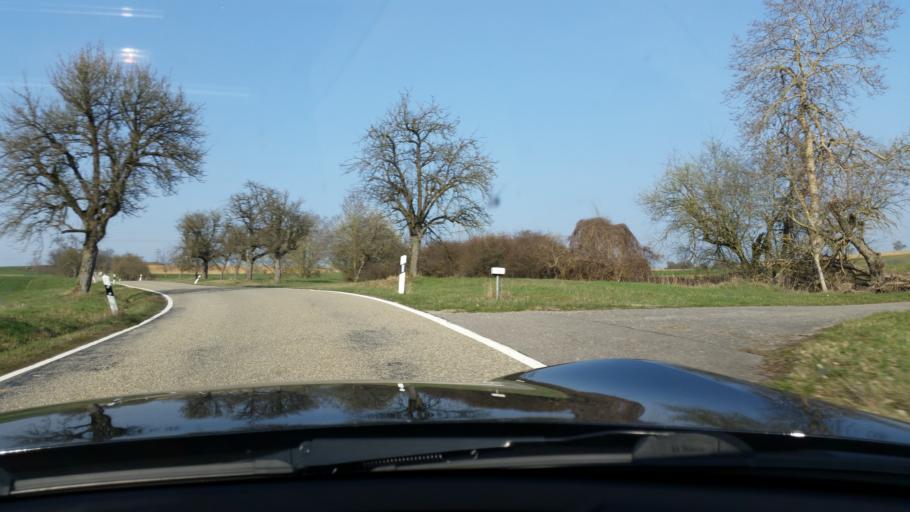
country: DE
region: Baden-Wuerttemberg
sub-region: Regierungsbezirk Stuttgart
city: Mockmuhl
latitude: 49.3302
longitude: 9.3655
